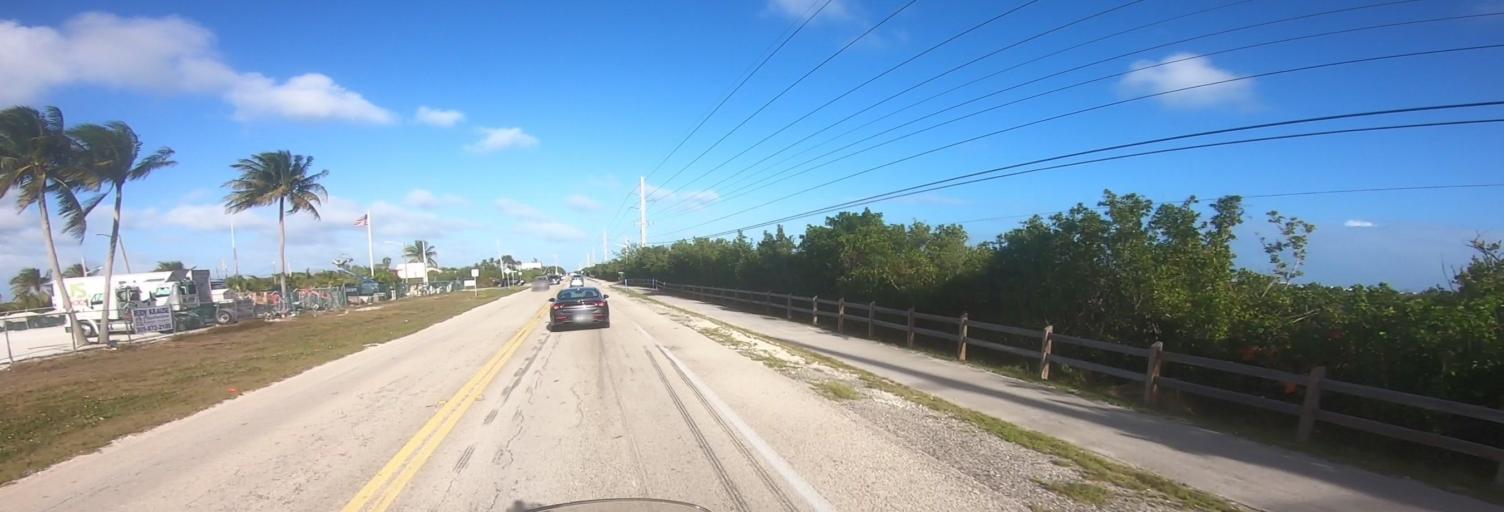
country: US
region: Florida
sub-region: Monroe County
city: Big Pine Key
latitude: 24.6599
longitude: -81.4169
